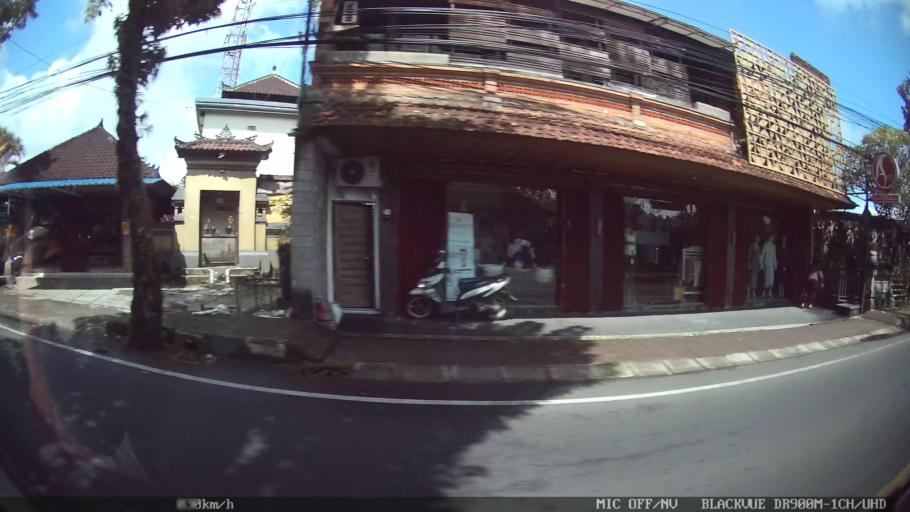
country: ID
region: Bali
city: Banjar Tebongkang
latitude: -8.5463
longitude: 115.2719
